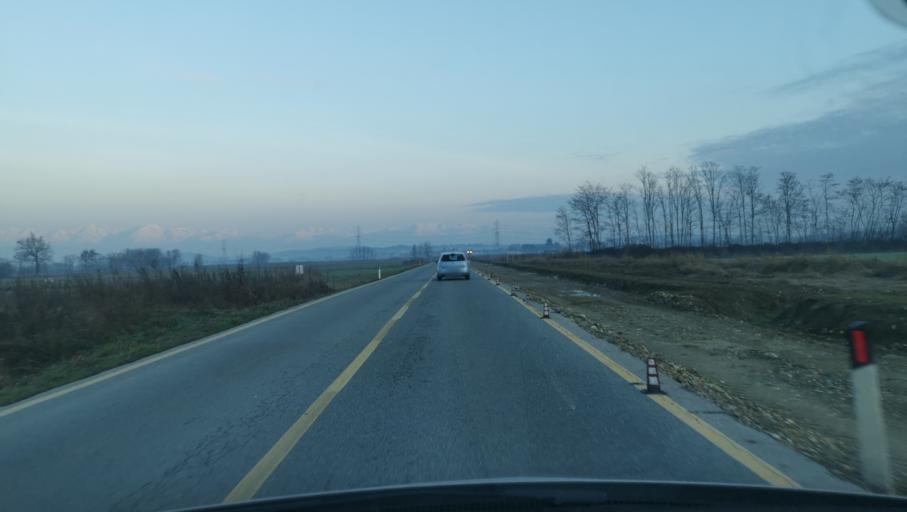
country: IT
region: Piedmont
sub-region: Provincia di Torino
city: Caluso
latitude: 45.2687
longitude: 7.8923
